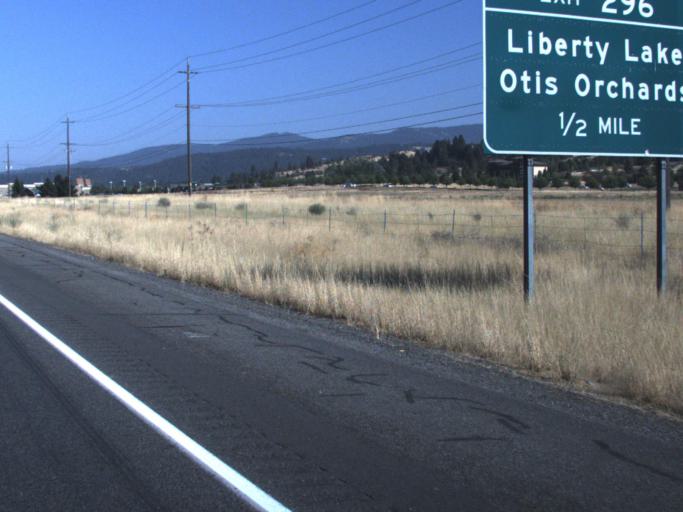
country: US
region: Washington
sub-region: Spokane County
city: Liberty Lake
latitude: 47.6666
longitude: -117.1255
